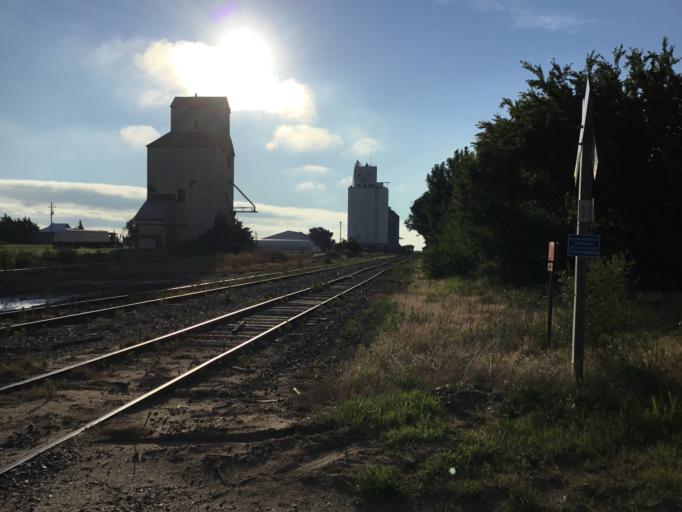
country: US
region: Kansas
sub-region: Barber County
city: Medicine Lodge
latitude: 37.4414
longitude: -98.4239
